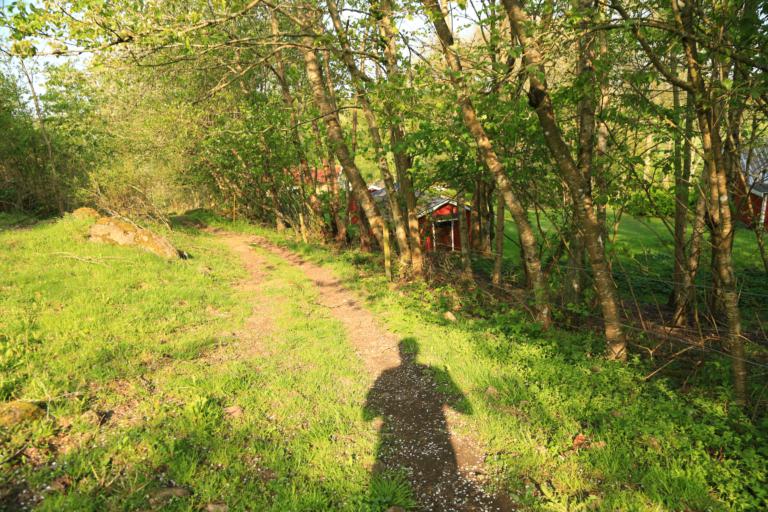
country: SE
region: Halland
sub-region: Varbergs Kommun
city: Varberg
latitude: 57.1592
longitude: 12.2388
